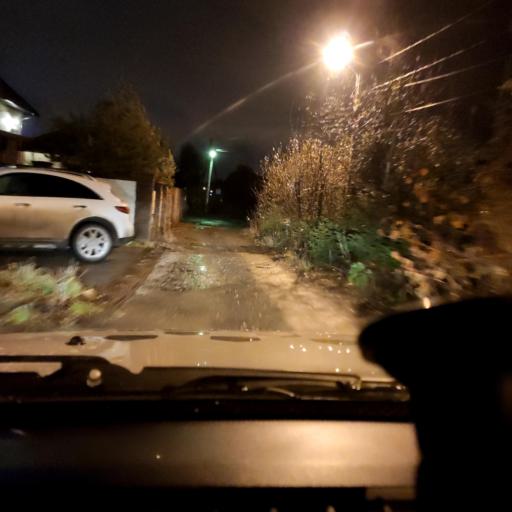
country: RU
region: Perm
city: Perm
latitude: 57.9789
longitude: 56.3125
